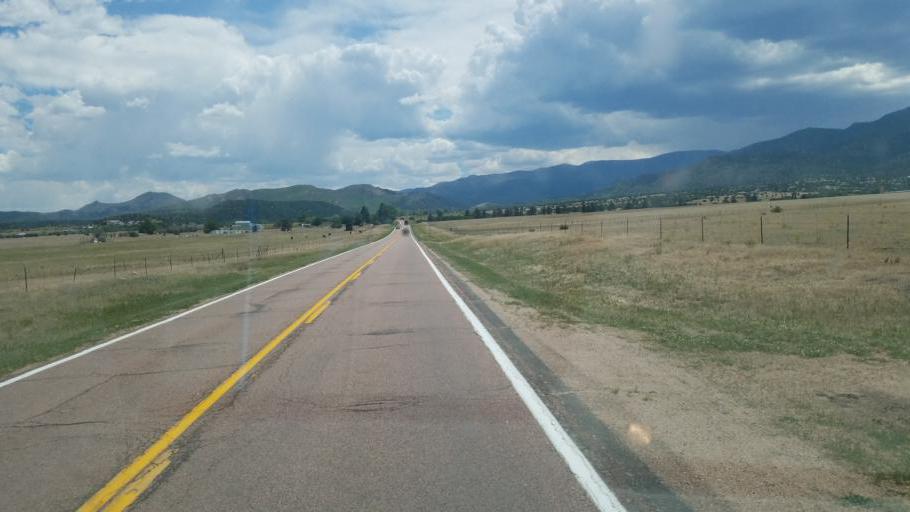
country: US
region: Colorado
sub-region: Fremont County
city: Florence
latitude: 38.2519
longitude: -105.0902
